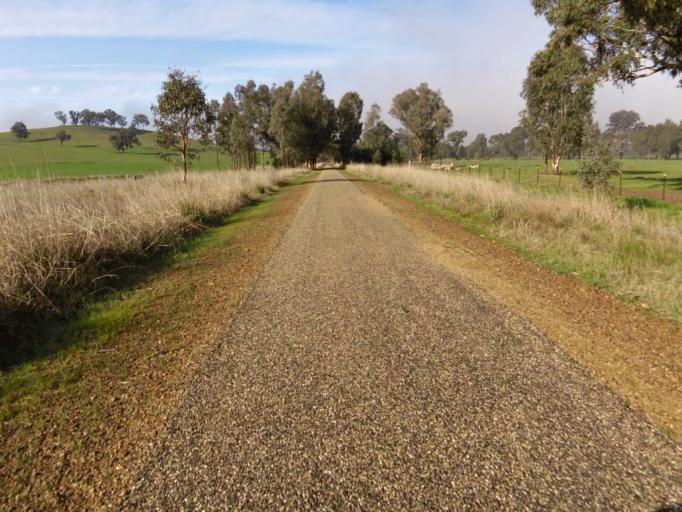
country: AU
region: Victoria
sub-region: Wangaratta
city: Wangaratta
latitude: -36.4423
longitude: 146.5511
